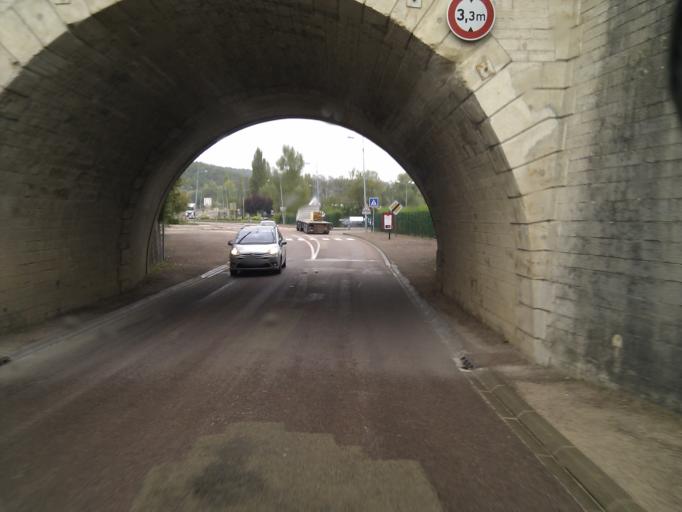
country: FR
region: Bourgogne
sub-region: Departement de la Cote-d'Or
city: Montbard
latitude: 47.6214
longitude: 4.3230
